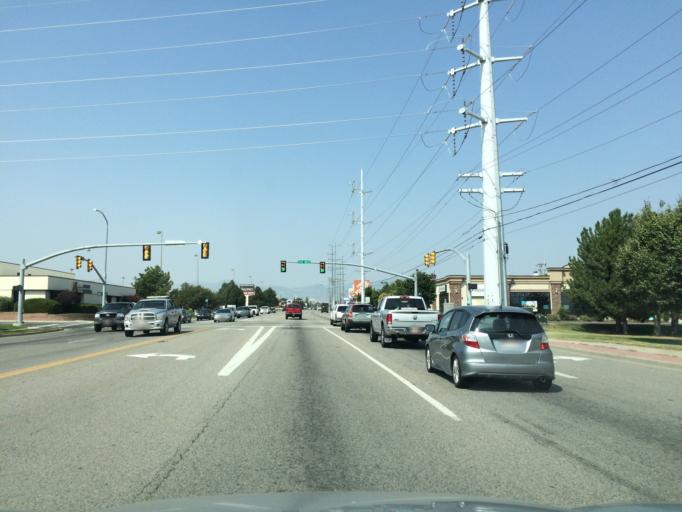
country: US
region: Utah
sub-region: Salt Lake County
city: West Jordan
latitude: 40.5878
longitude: -111.9333
